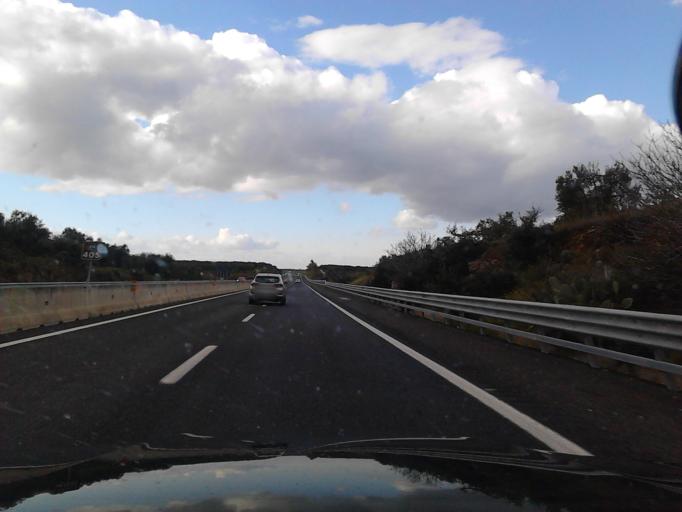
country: IT
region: Apulia
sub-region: Provincia di Barletta - Andria - Trani
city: Andria
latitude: 41.2601
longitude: 16.2645
